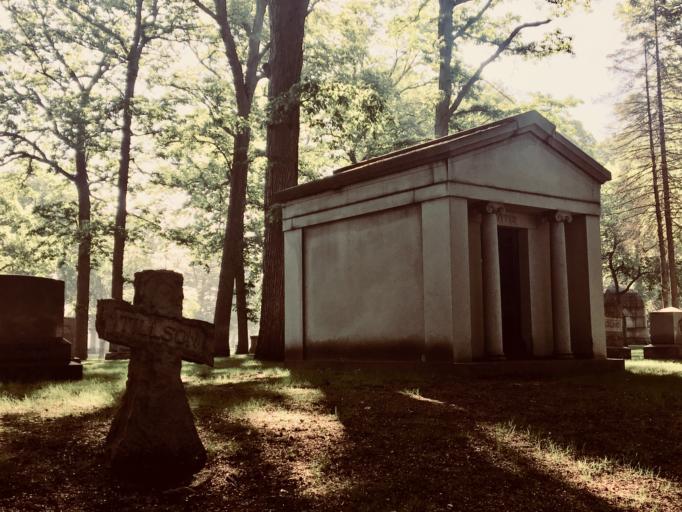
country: US
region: Michigan
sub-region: Oakland County
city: Ferndale
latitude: 42.4412
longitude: -83.1243
